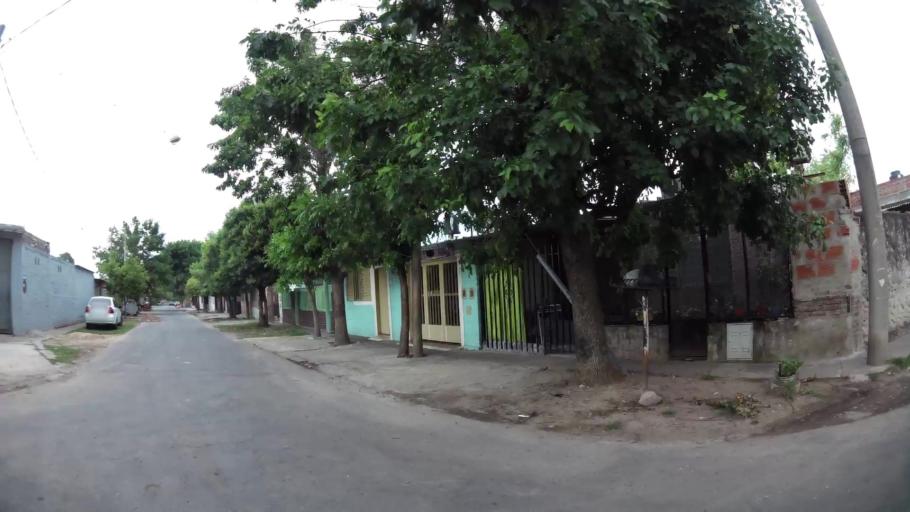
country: AR
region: Santa Fe
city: Gobernador Galvez
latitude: -33.0010
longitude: -60.6873
